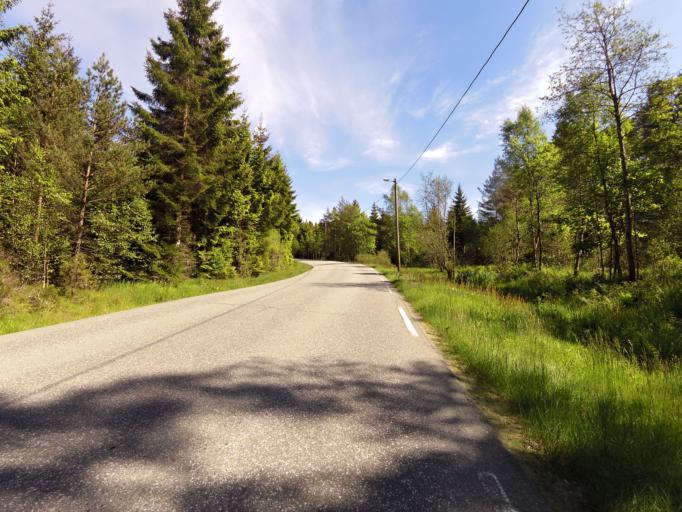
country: NO
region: Hordaland
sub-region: Stord
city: Sagvag
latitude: 59.7909
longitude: 5.4334
